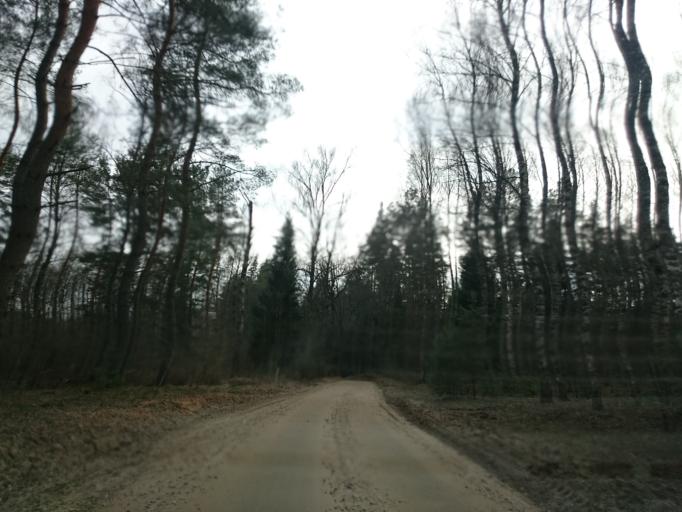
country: LV
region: Garkalne
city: Garkalne
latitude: 57.0237
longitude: 24.3866
